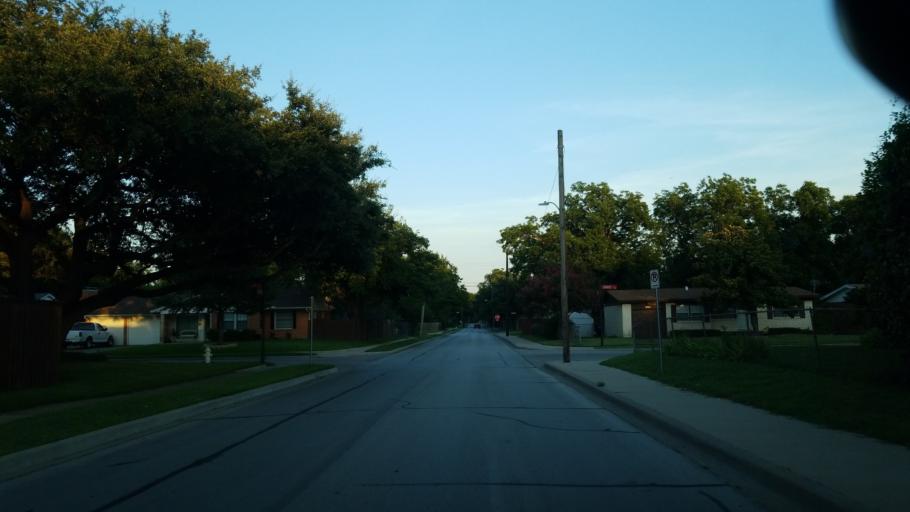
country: US
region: Texas
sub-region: Dallas County
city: Farmers Branch
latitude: 32.9351
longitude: -96.8846
